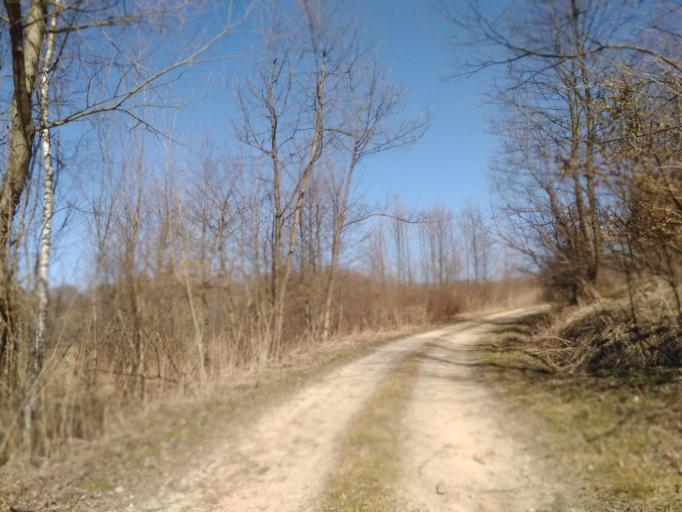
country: PL
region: Subcarpathian Voivodeship
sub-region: Powiat brzozowski
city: Blizne
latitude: 49.7249
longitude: 21.9738
